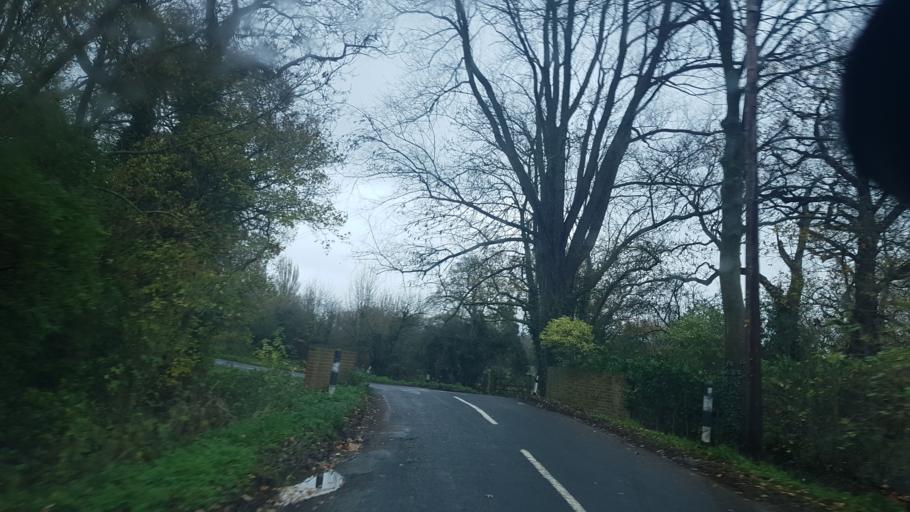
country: GB
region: England
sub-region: Surrey
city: Ripley
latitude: 51.2782
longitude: -0.4974
